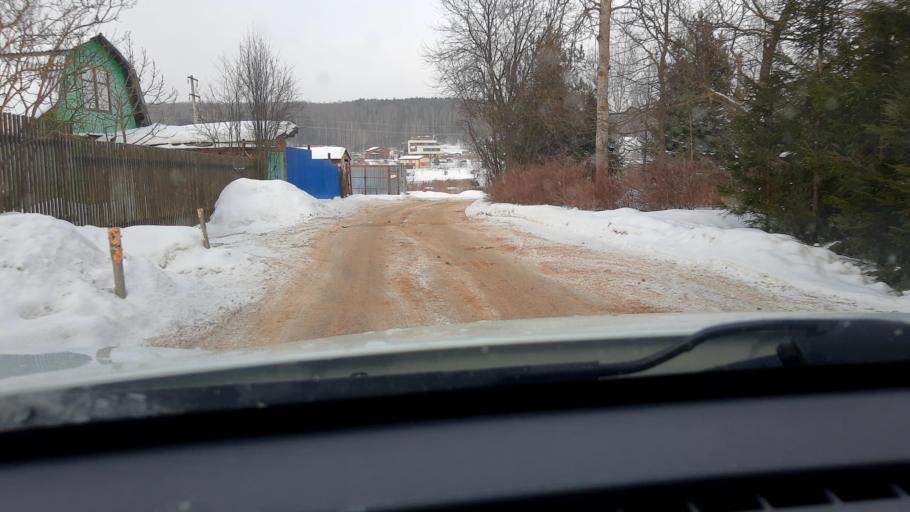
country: RU
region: Moskovskaya
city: Pavlovskaya Sloboda
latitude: 55.8220
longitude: 37.0941
